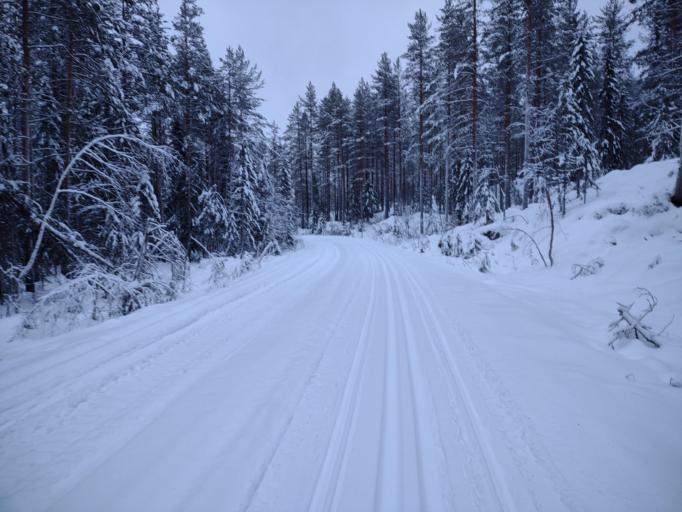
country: NO
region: Buskerud
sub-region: Flesberg
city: Lampeland
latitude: 59.7227
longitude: 9.5423
